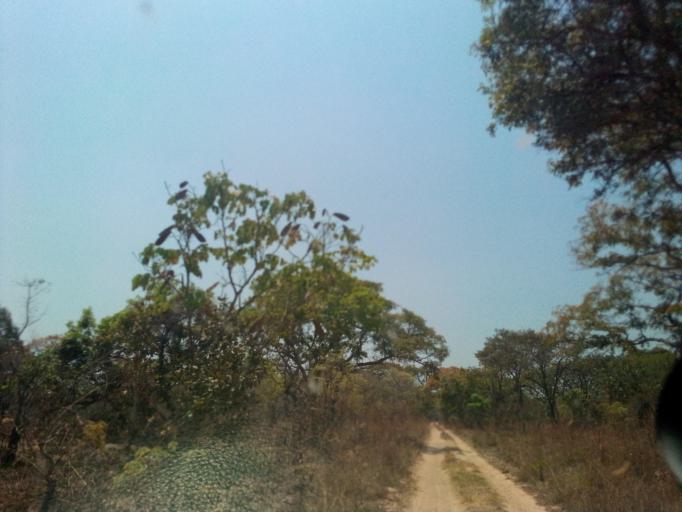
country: ZM
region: Copperbelt
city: Kataba
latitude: -12.2454
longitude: 30.3968
